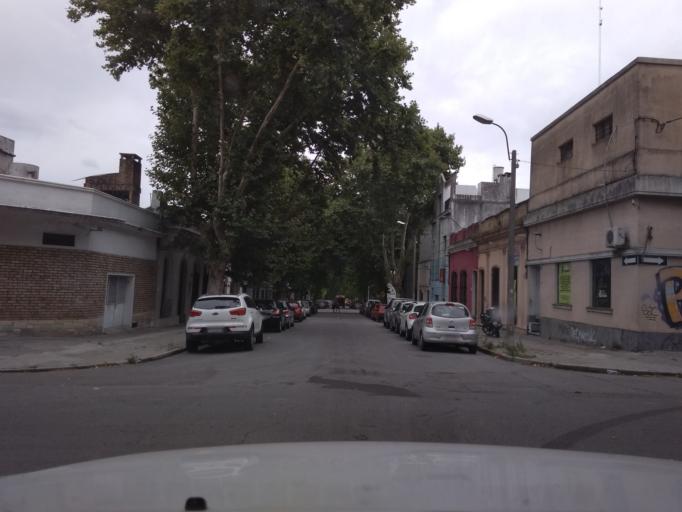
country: UY
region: Montevideo
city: Montevideo
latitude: -34.8956
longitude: -56.1831
